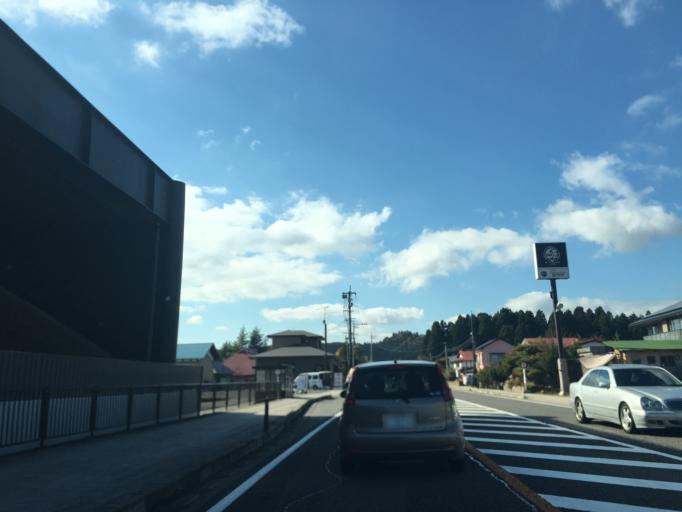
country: JP
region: Fukushima
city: Inawashiro
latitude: 37.5363
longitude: 140.0736
